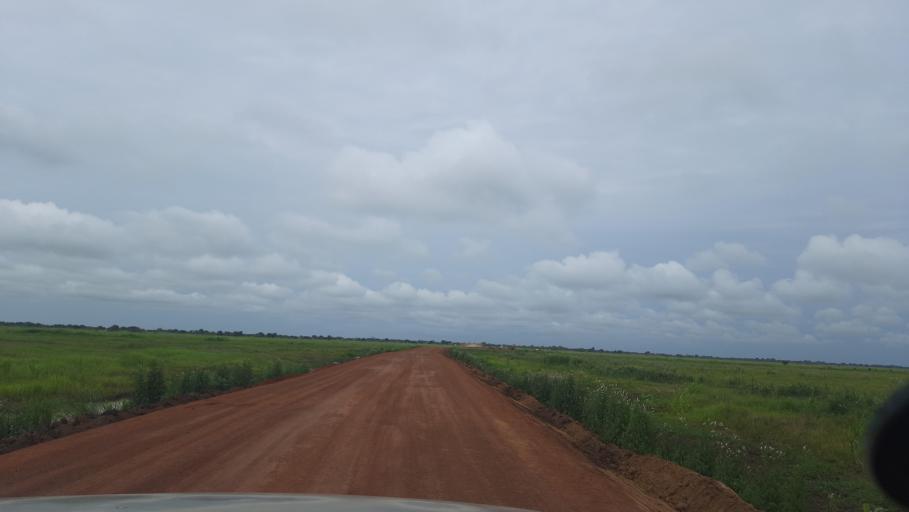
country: ET
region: Gambela
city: Gambela
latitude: 8.3434
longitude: 33.7801
